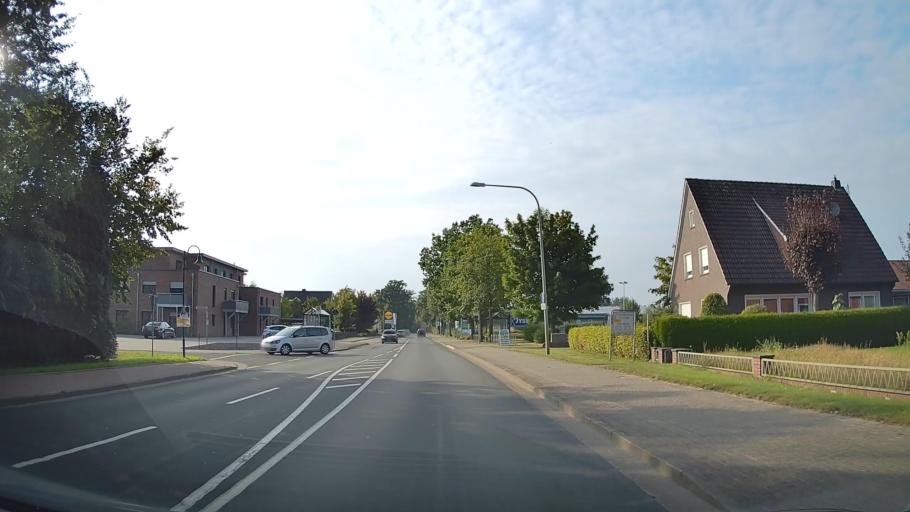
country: DE
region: Lower Saxony
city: Barssel
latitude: 53.1628
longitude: 7.7536
